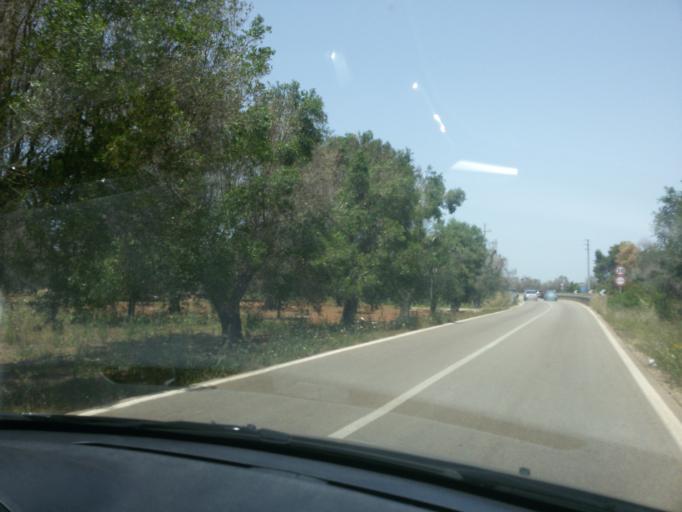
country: IT
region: Apulia
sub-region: Provincia di Lecce
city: Veglie
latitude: 40.3251
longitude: 17.9252
